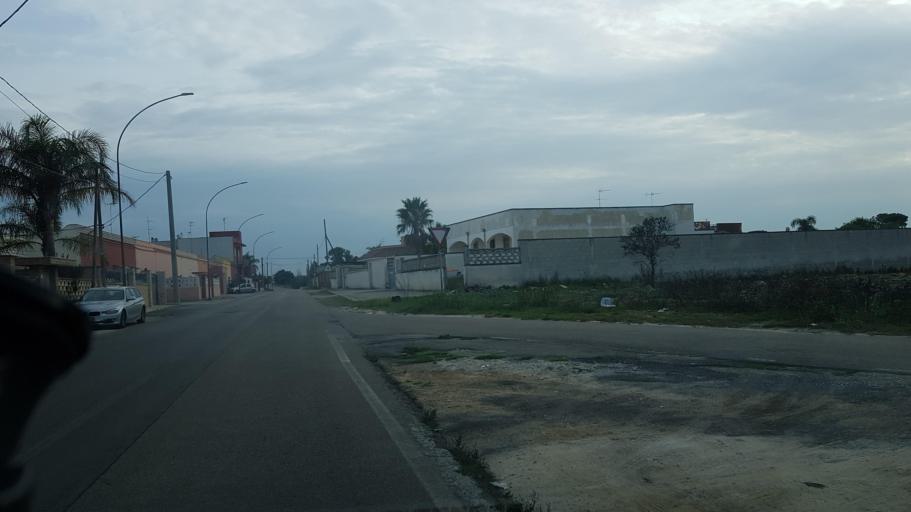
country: IT
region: Apulia
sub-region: Provincia di Lecce
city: Trepuzzi
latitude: 40.4167
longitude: 18.0734
